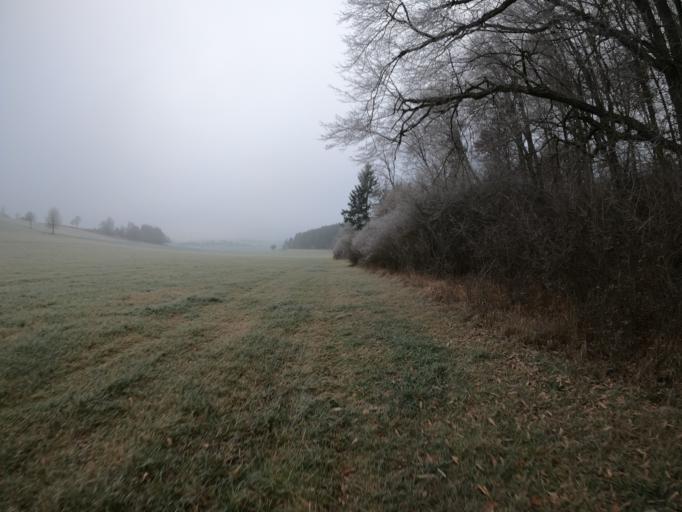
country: DE
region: Baden-Wuerttemberg
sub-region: Tuebingen Region
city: Westerstetten
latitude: 48.4975
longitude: 9.9578
